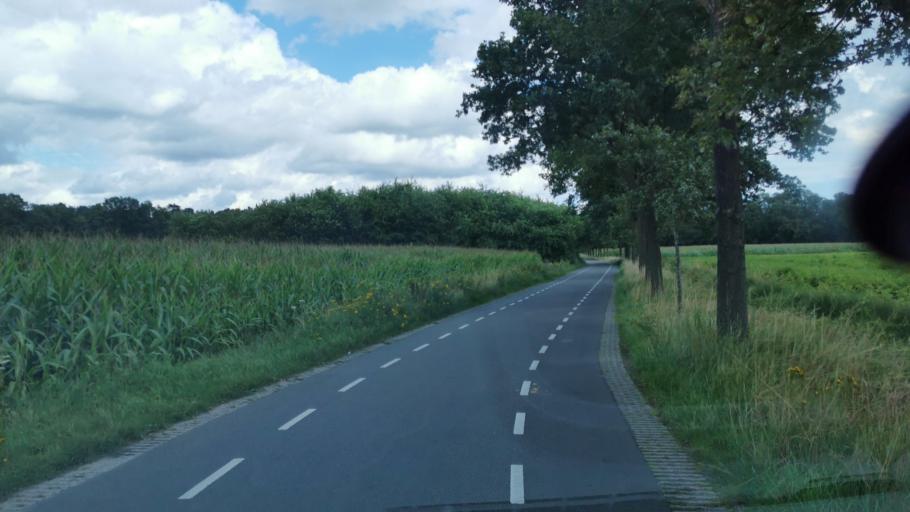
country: NL
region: Overijssel
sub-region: Gemeente Haaksbergen
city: Haaksbergen
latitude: 52.1471
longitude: 6.8005
